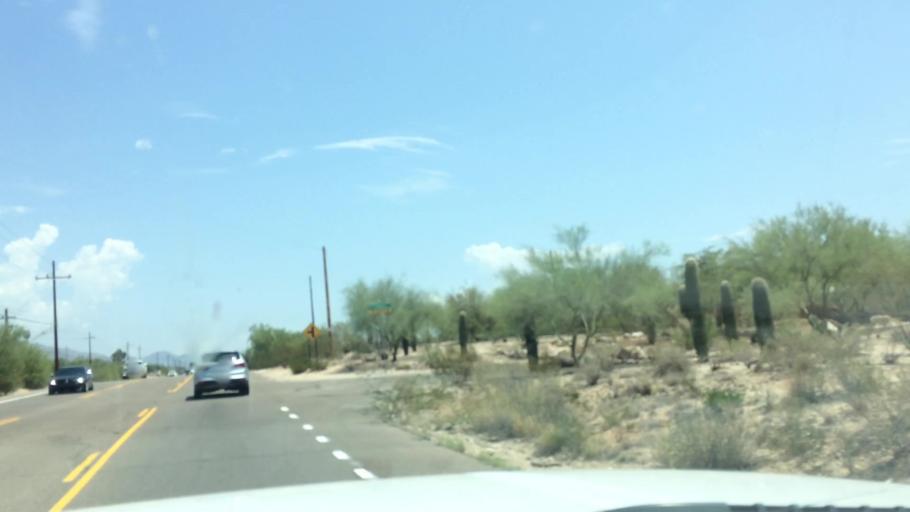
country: US
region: Arizona
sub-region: Pima County
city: Casas Adobes
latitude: 32.3231
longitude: -111.0024
